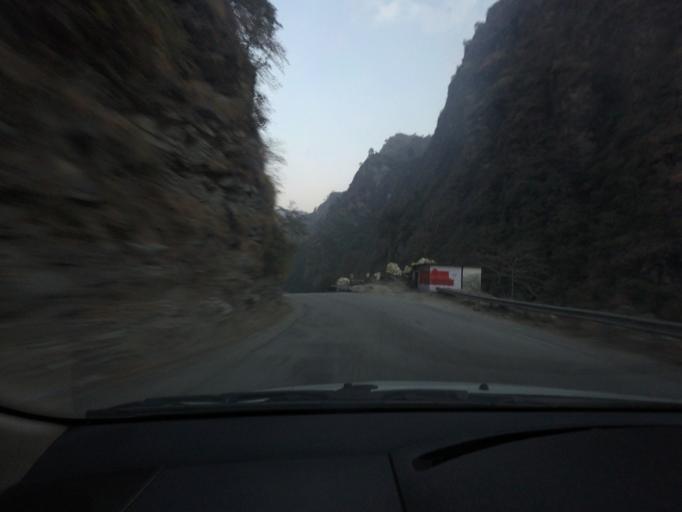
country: IN
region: Himachal Pradesh
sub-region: Mandi
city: Pandoh
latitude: 31.6950
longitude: 77.1415
